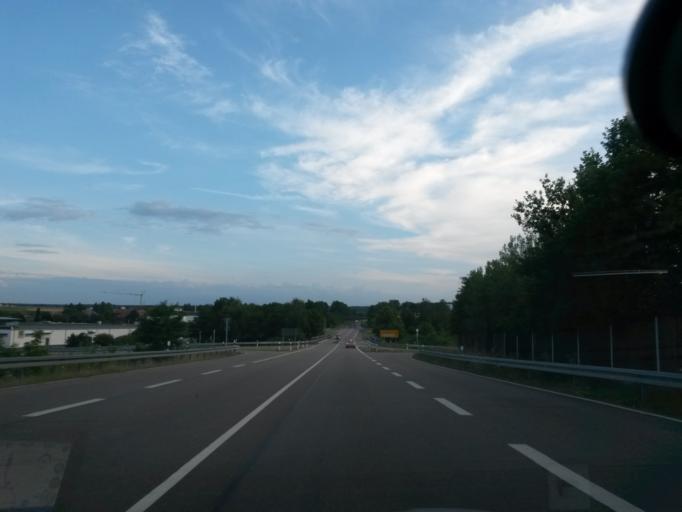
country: DE
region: Bavaria
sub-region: Upper Palatinate
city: Amberg
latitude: 49.4476
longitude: 11.8346
